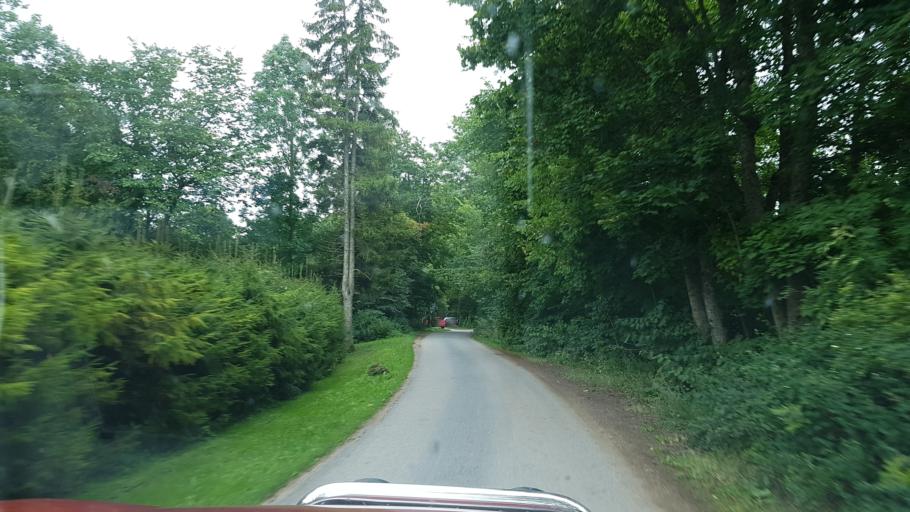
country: EE
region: Laeaene
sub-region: Ridala Parish
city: Uuemoisa
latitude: 58.7887
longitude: 23.6628
